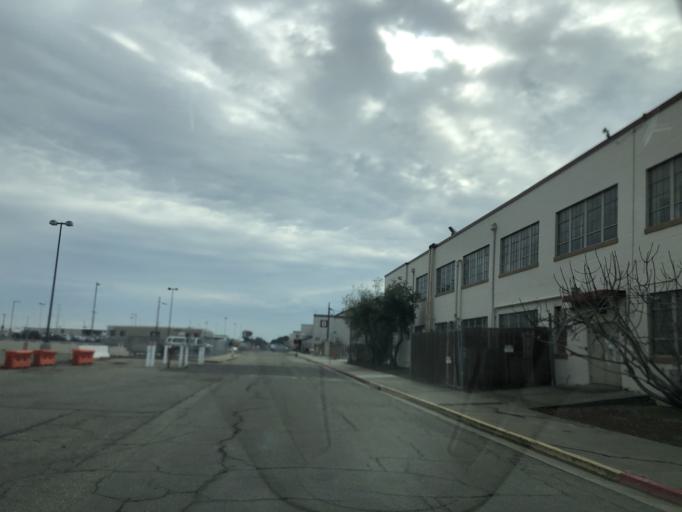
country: US
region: California
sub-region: Alameda County
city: Alameda
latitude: 37.7371
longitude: -122.2173
